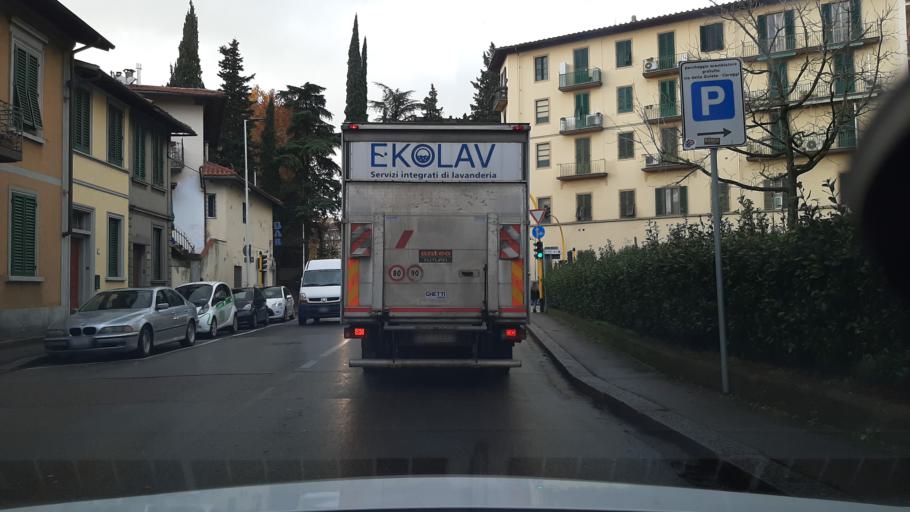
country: IT
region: Tuscany
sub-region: Province of Florence
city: Florence
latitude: 43.8048
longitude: 11.2418
